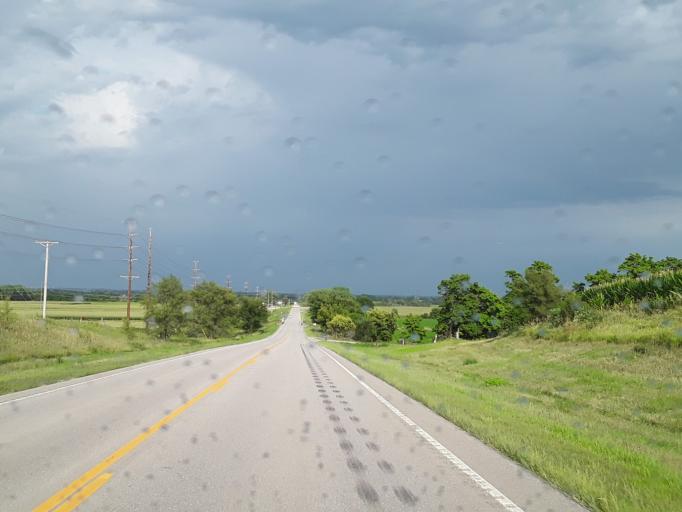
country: US
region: Nebraska
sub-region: Saunders County
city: Ashland
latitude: 41.0886
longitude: -96.3846
